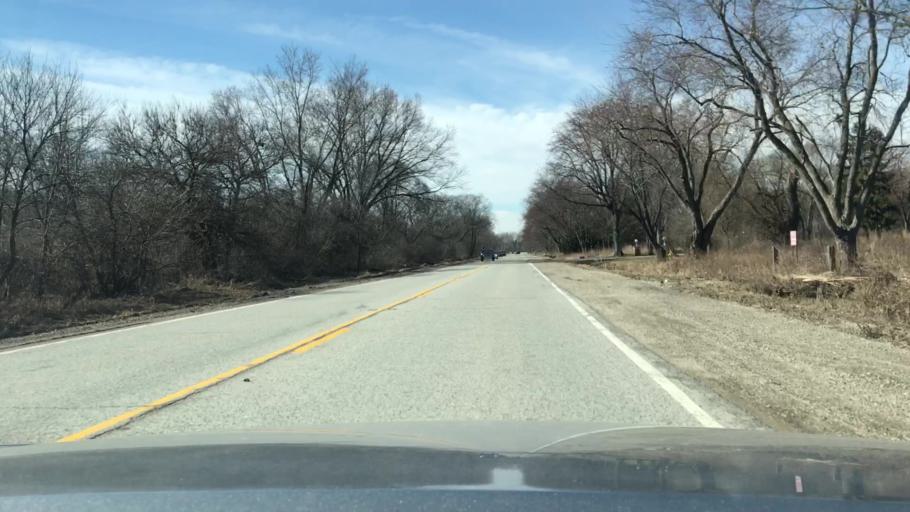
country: US
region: Illinois
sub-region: DuPage County
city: Lisle
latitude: 41.8239
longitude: -88.0569
